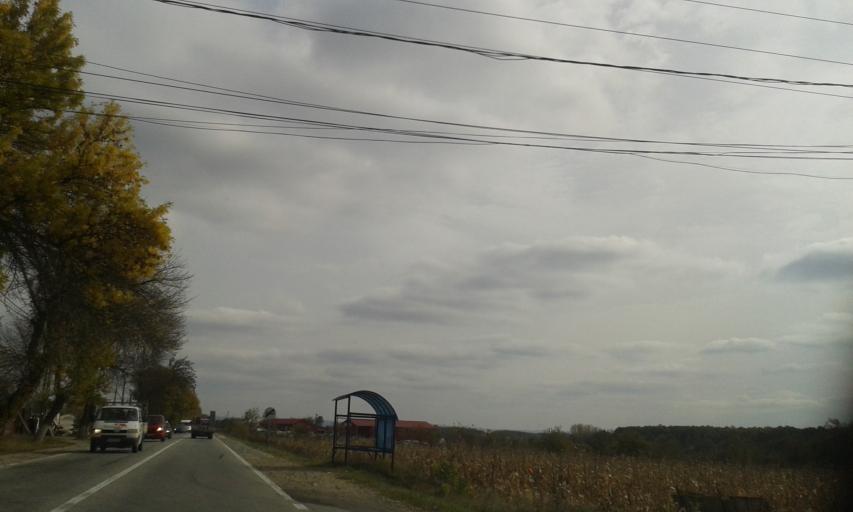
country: RO
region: Gorj
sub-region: Comuna Scoarta
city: Scoarta
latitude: 45.0297
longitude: 23.4219
